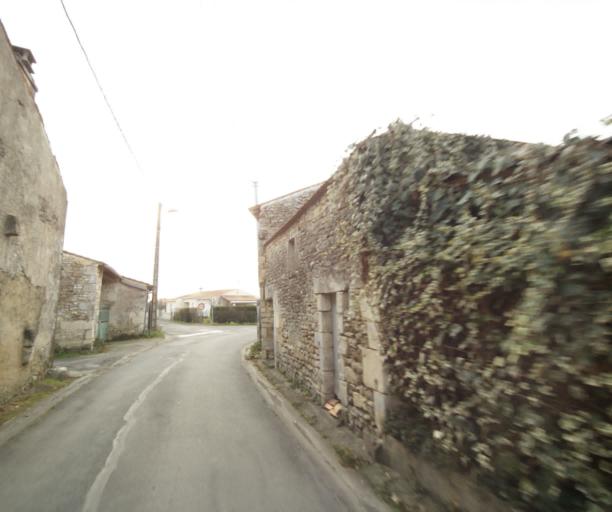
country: FR
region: Poitou-Charentes
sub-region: Departement de la Charente-Maritime
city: Fontcouverte
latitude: 45.7780
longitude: -0.6063
